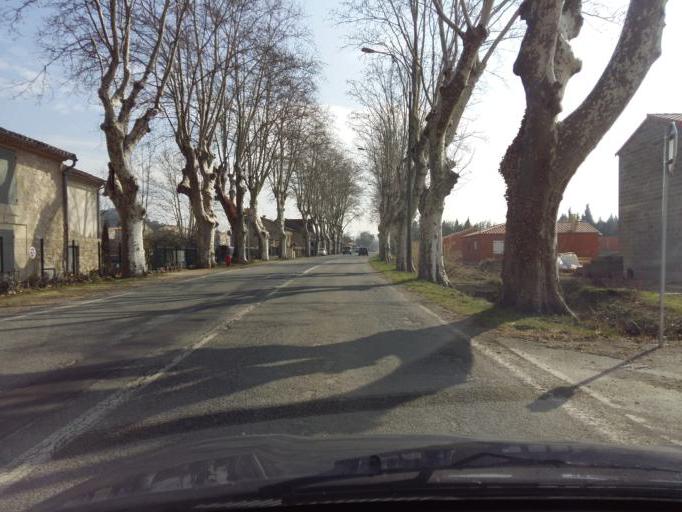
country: FR
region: Provence-Alpes-Cote d'Azur
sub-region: Departement des Bouches-du-Rhone
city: Orgon
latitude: 43.8063
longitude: 4.9975
